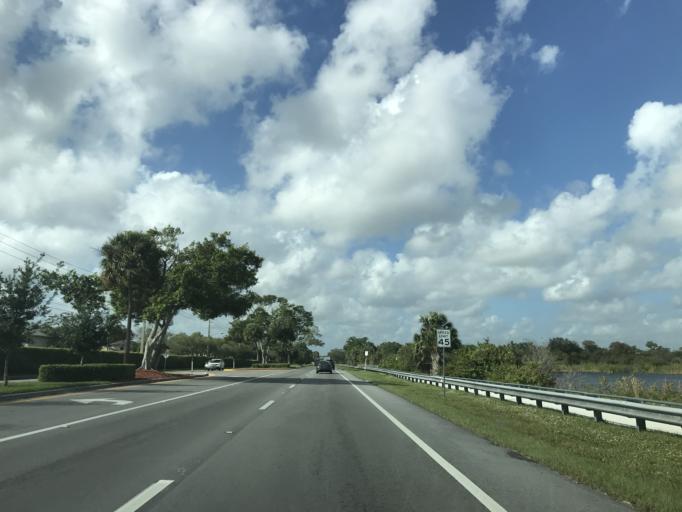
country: US
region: Florida
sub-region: Broward County
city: Coconut Creek
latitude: 26.2600
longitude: -80.1689
